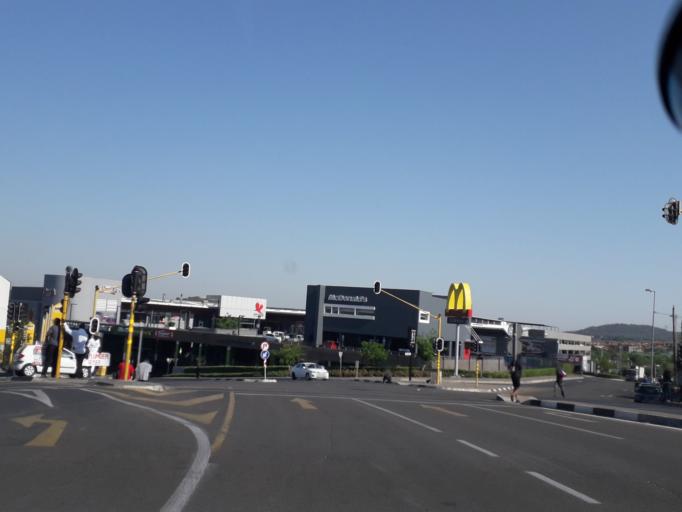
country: ZA
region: Gauteng
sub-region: City of Johannesburg Metropolitan Municipality
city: Midrand
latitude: -26.0311
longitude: 28.0629
